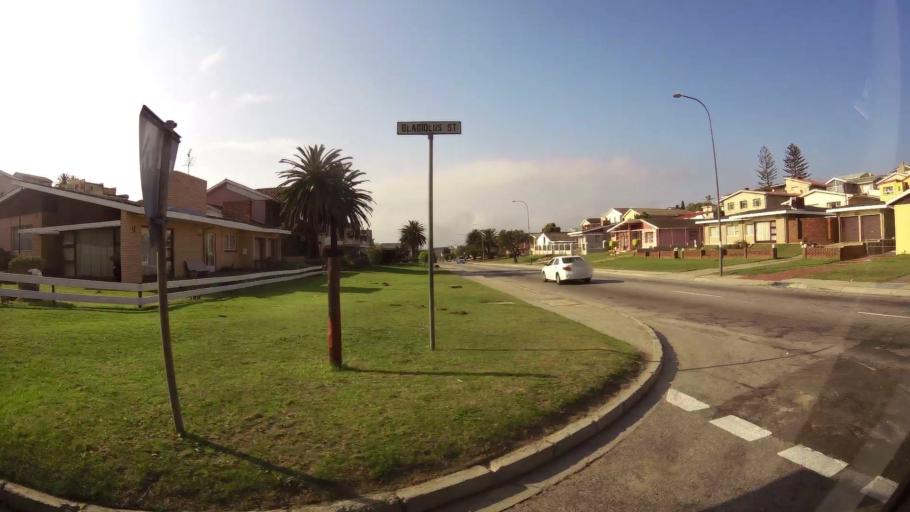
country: ZA
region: Eastern Cape
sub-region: Nelson Mandela Bay Metropolitan Municipality
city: Port Elizabeth
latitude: -33.9261
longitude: 25.5420
